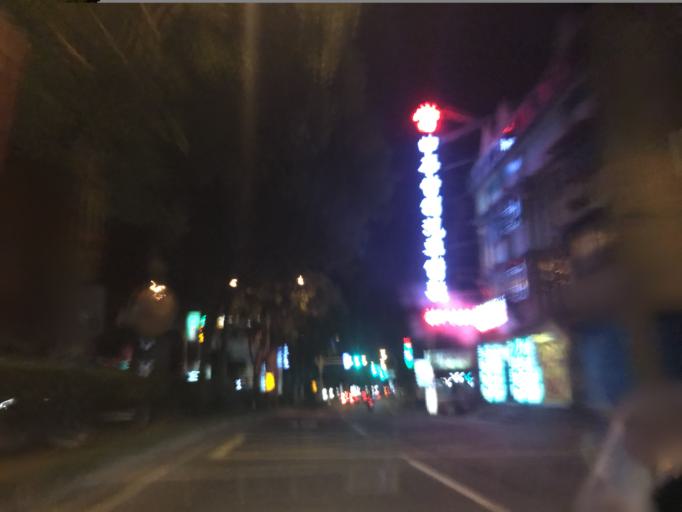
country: TW
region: Taiwan
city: Daxi
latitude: 24.8762
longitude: 121.2130
